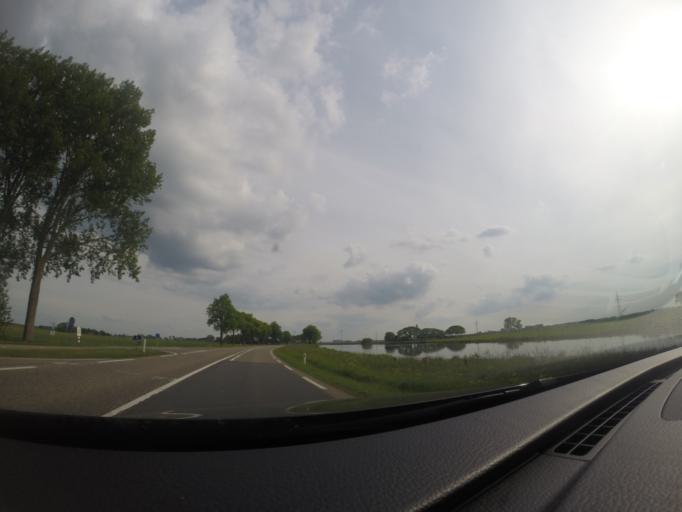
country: NL
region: Flevoland
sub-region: Gemeente Noordoostpolder
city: Ens
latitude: 52.5997
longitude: 5.8664
